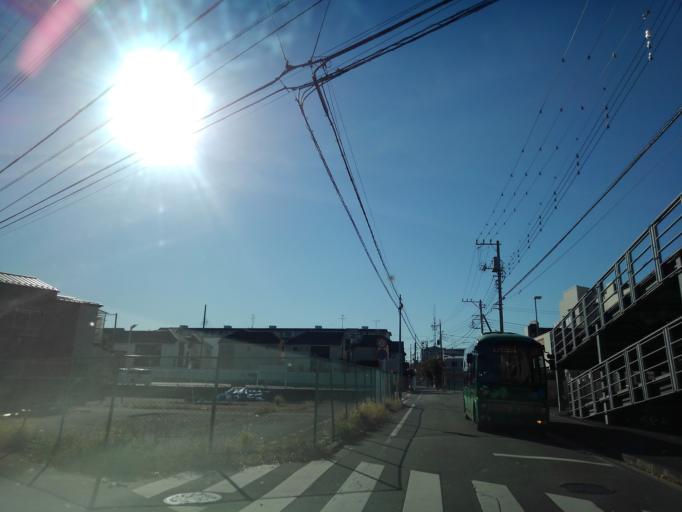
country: JP
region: Tokyo
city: Higashimurayama-shi
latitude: 35.7606
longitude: 139.4687
